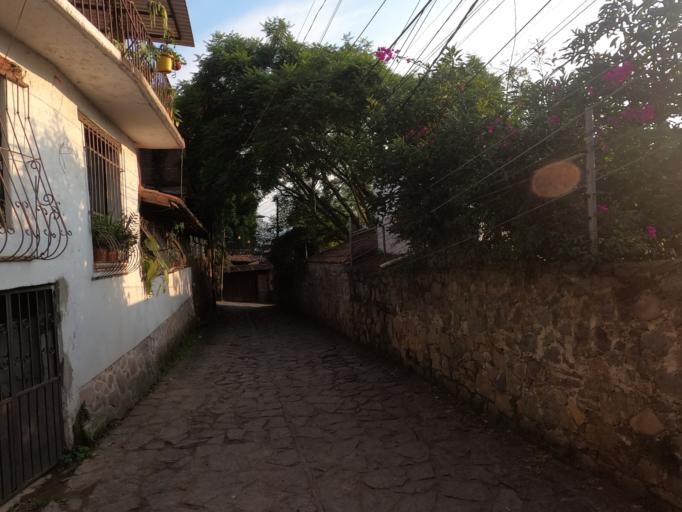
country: MX
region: Mexico
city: Valle de Bravo
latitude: 19.1943
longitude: -100.1283
